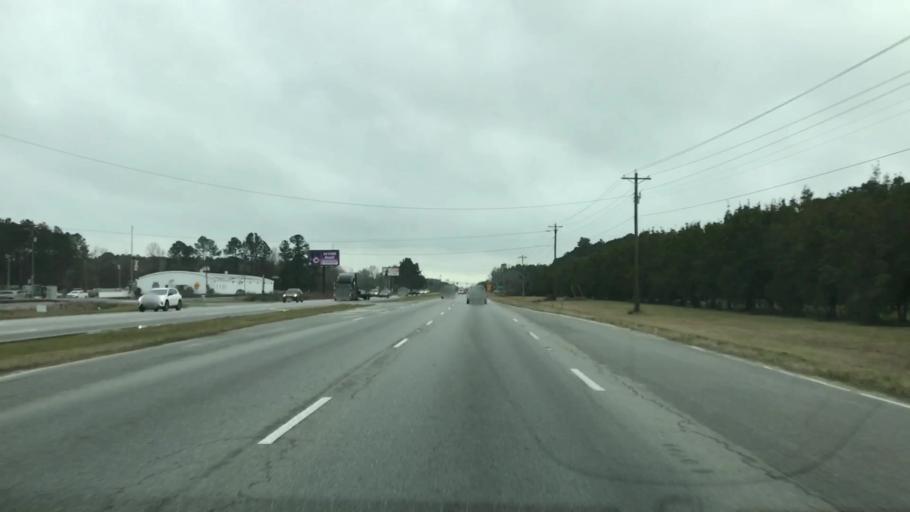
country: US
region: South Carolina
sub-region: Berkeley County
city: Goose Creek
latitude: 33.0381
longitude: -80.0338
